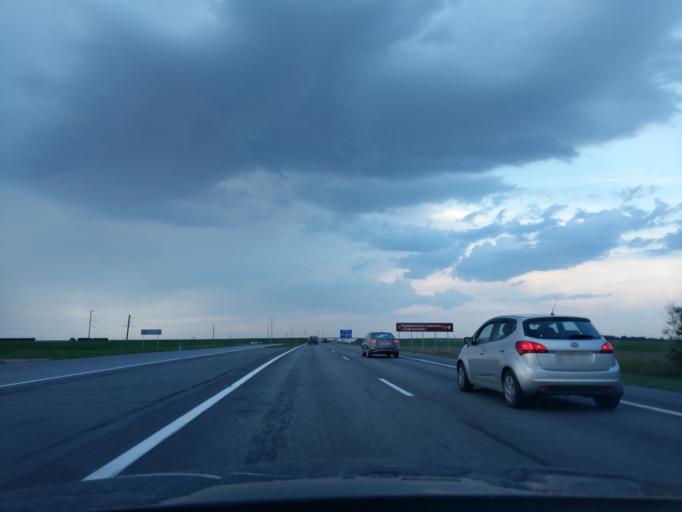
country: BY
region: Minsk
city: Stowbtsy
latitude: 53.5139
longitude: 26.6801
